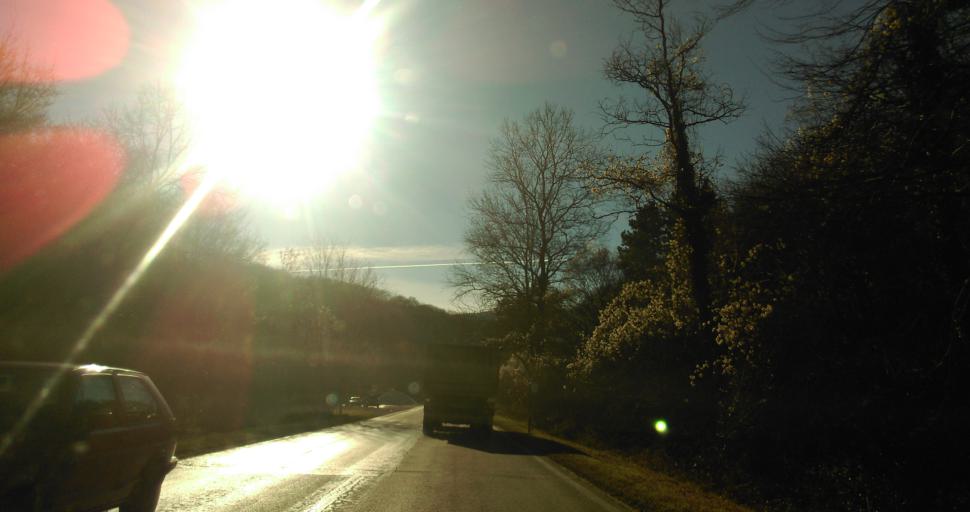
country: RS
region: Autonomna Pokrajina Vojvodina
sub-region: Juznobacki Okrug
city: Novi Sad
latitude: 45.1816
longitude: 19.8391
